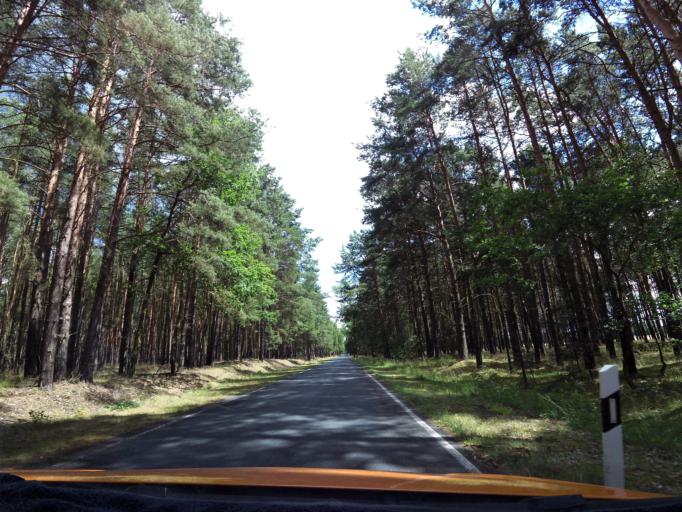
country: DE
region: Brandenburg
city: Storkow
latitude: 52.2456
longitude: 13.8463
